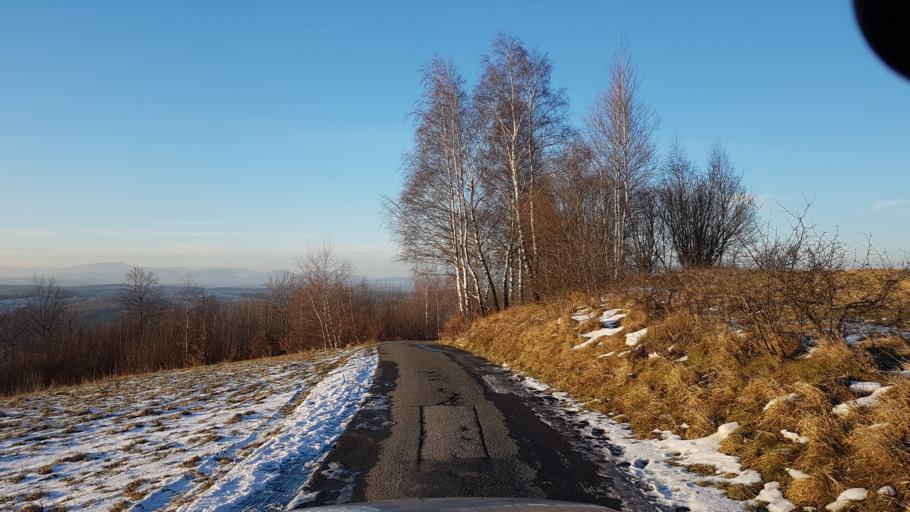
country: PL
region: Lesser Poland Voivodeship
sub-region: Powiat nowosadecki
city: Rytro
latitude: 49.5083
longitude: 20.6729
